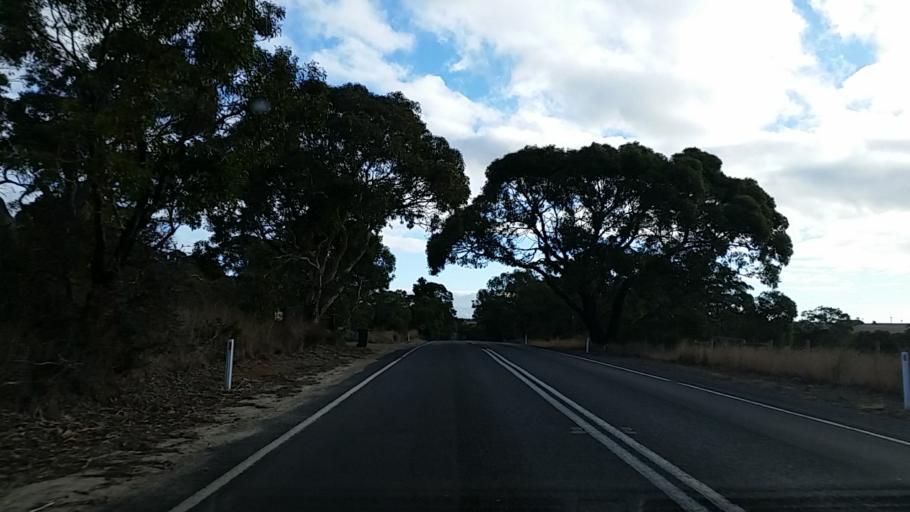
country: AU
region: South Australia
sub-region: Yankalilla
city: Normanville
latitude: -35.5661
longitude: 138.2032
